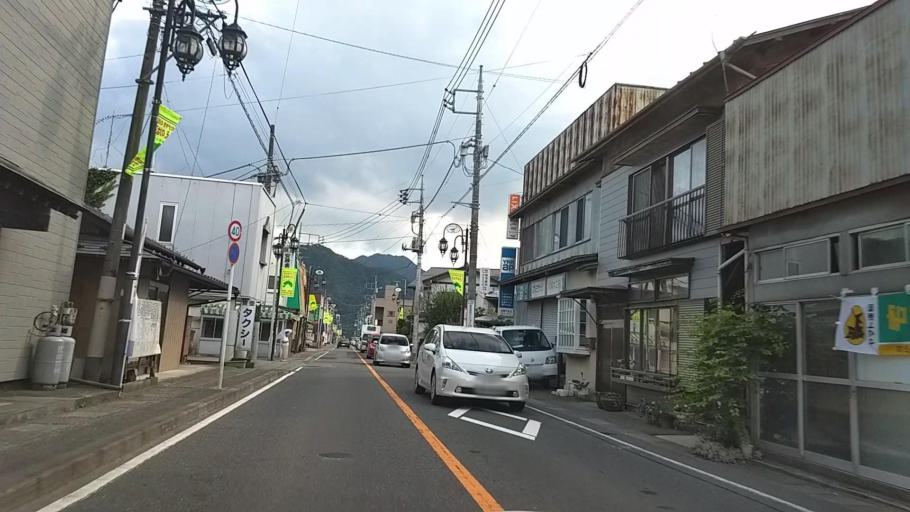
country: JP
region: Yamanashi
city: Uenohara
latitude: 35.6248
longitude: 139.1159
